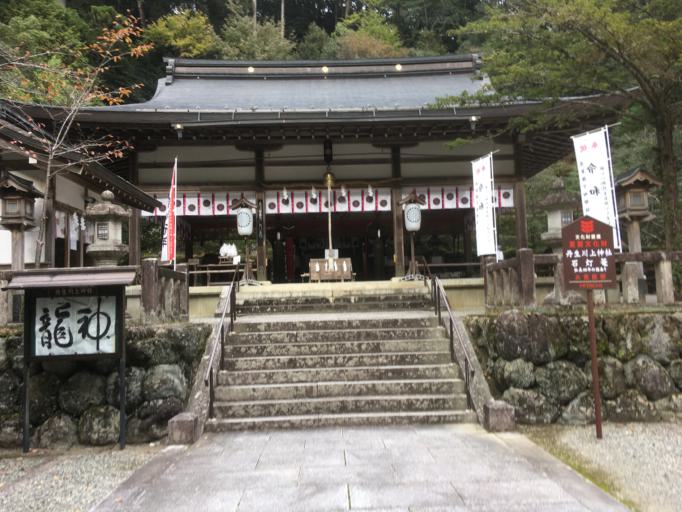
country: JP
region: Nara
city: Yoshino-cho
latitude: 34.3900
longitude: 135.9863
